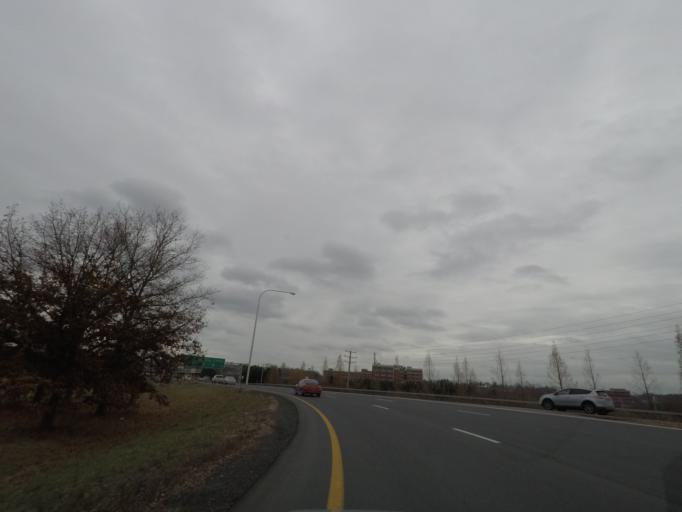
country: US
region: New York
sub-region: Schenectady County
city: Scotia
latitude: 42.8136
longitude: -73.9564
